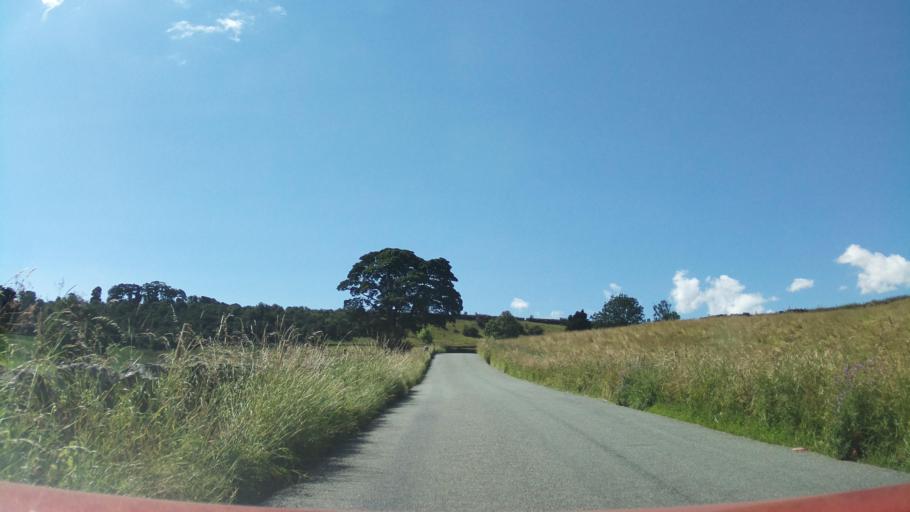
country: GB
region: England
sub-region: Derbyshire
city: Buxton
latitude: 53.1827
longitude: -1.8513
